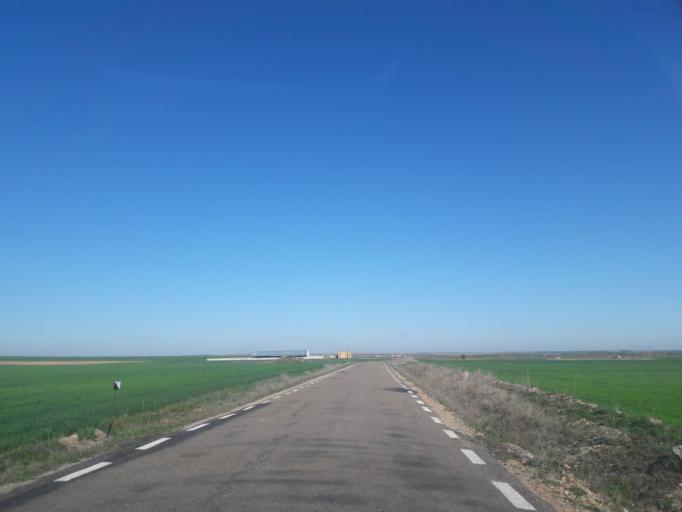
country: ES
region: Castille and Leon
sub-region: Provincia de Salamanca
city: Coca de Alba
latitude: 40.8644
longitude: -5.3706
